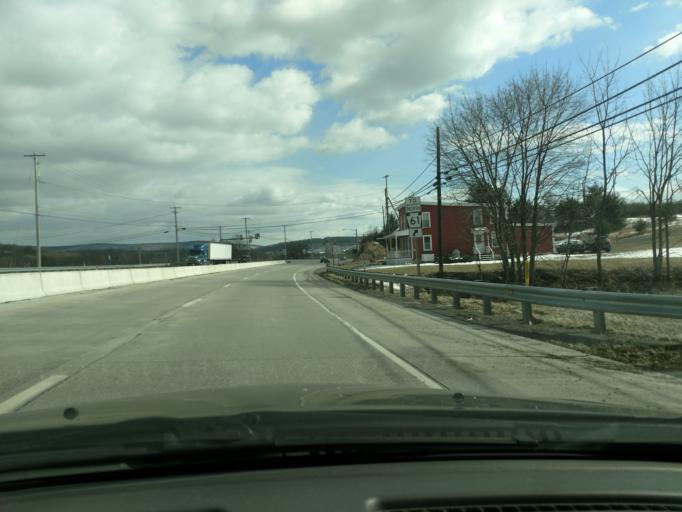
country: US
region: Pennsylvania
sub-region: Schuylkill County
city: Orwigsburg
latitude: 40.6320
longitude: -76.0649
